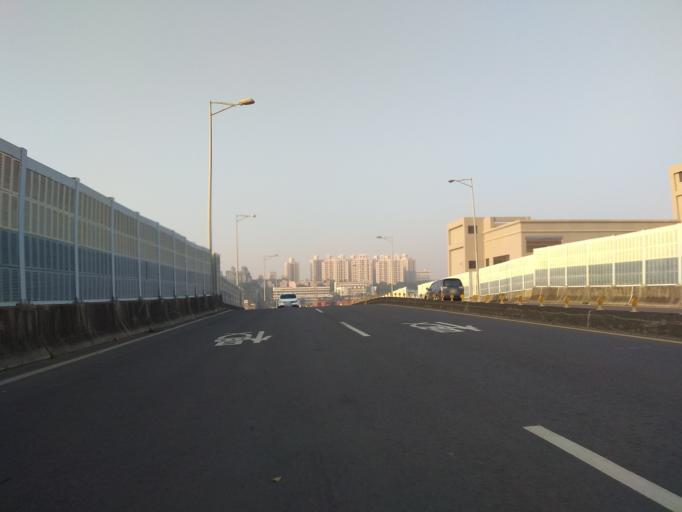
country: TW
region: Taiwan
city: Daxi
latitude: 24.9131
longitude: 121.1742
